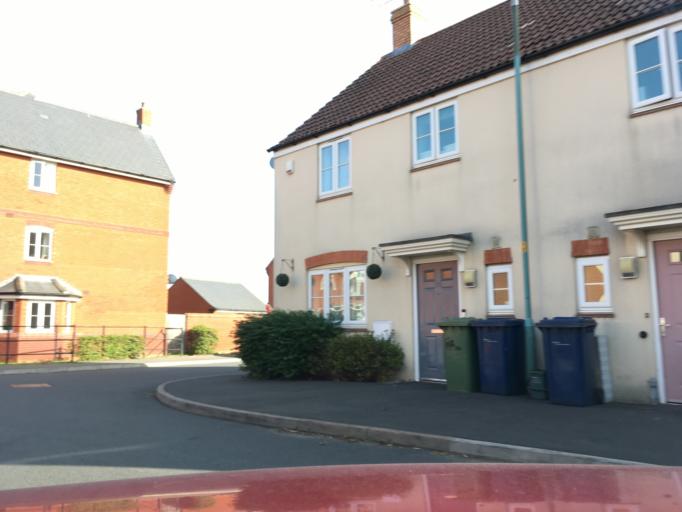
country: GB
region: England
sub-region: Gloucestershire
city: Tewkesbury
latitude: 51.9807
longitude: -2.1365
